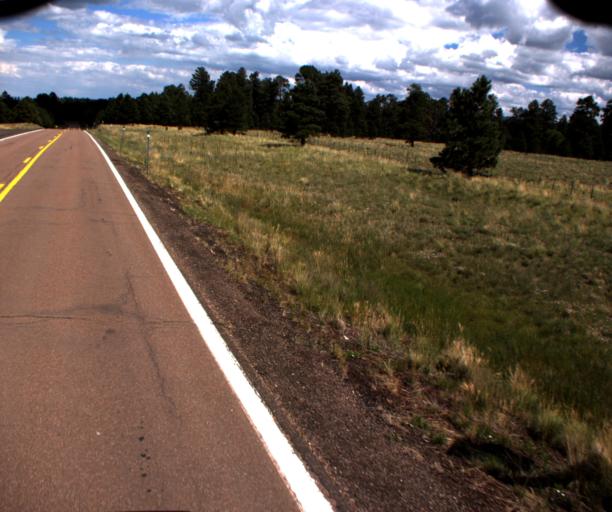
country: US
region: Arizona
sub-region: Apache County
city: Eagar
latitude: 34.0560
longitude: -109.5068
